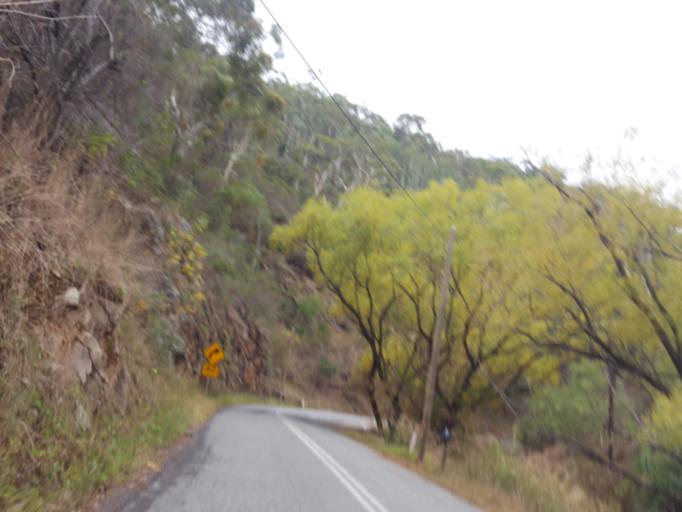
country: AU
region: South Australia
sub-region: Campbelltown
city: Athelstone
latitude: -34.8737
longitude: 138.7549
